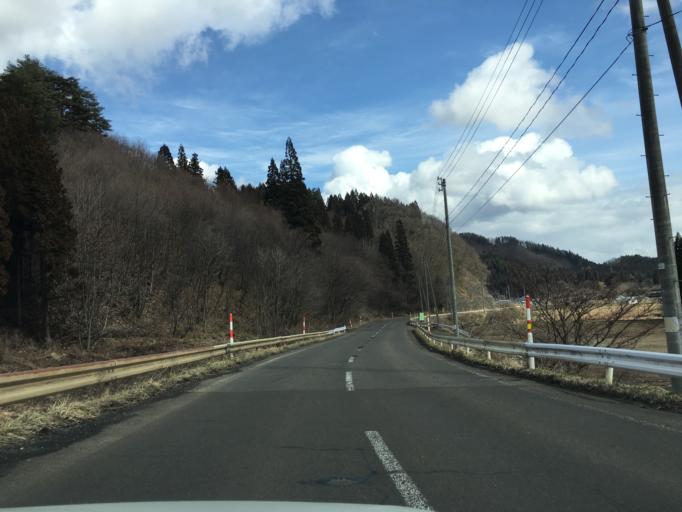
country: JP
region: Akita
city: Odate
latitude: 40.1943
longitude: 140.5289
